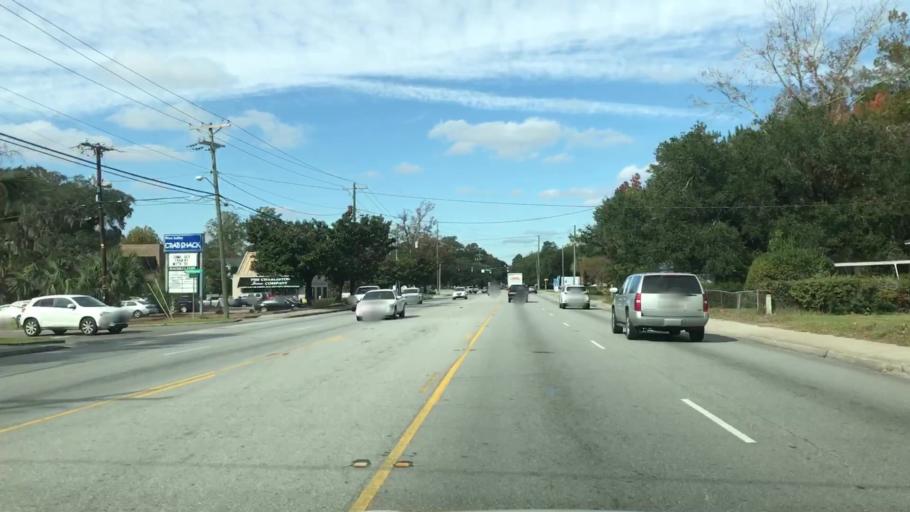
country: US
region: South Carolina
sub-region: Charleston County
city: North Charleston
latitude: 32.8056
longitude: -80.0213
